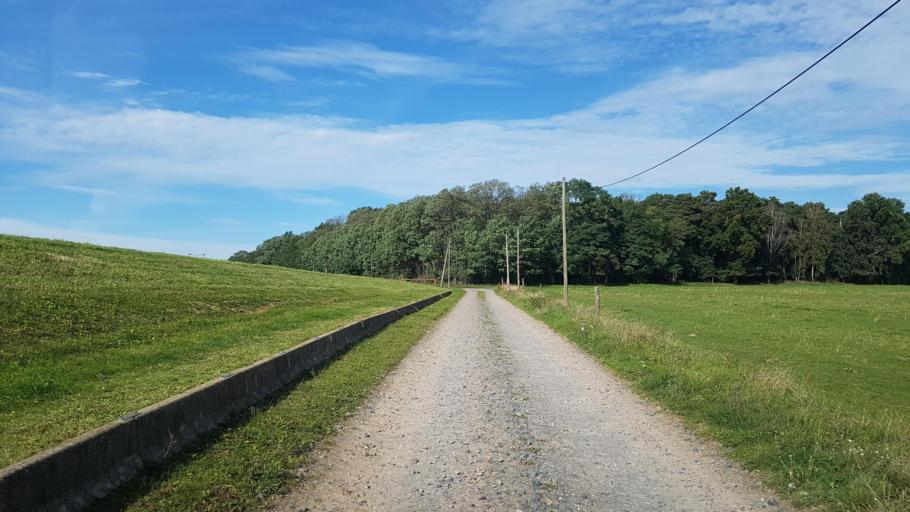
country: DE
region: Brandenburg
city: Juterbog
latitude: 51.9798
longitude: 13.0964
